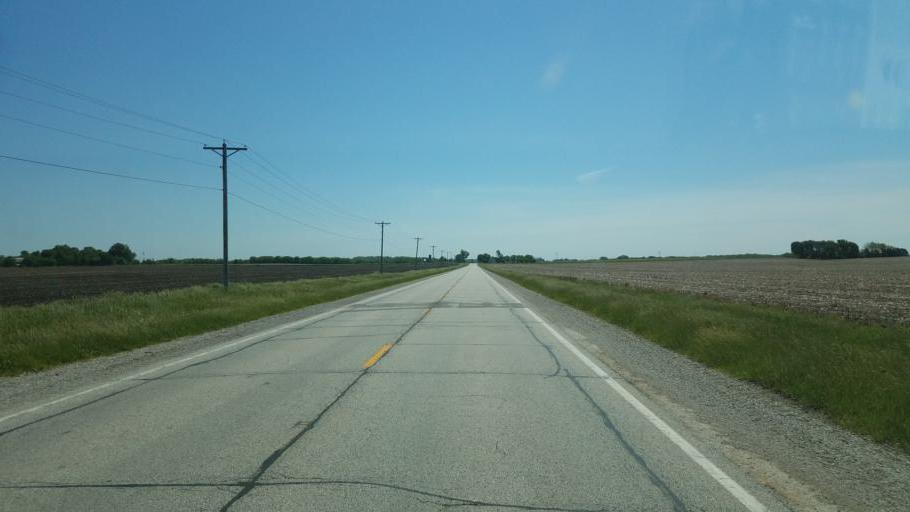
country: US
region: Illinois
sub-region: McLean County
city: Heyworth
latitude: 40.3121
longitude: -89.0457
